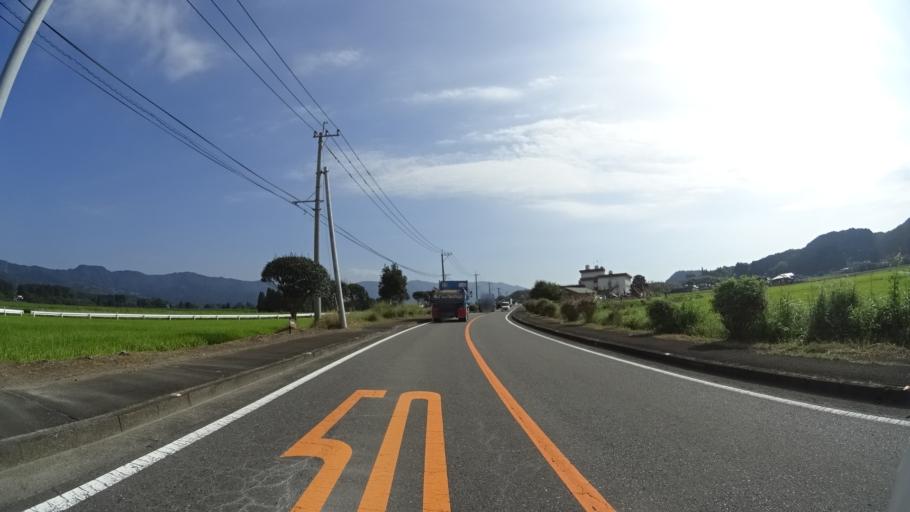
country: JP
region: Kagoshima
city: Okuchi-shinohara
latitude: 32.0370
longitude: 130.7497
